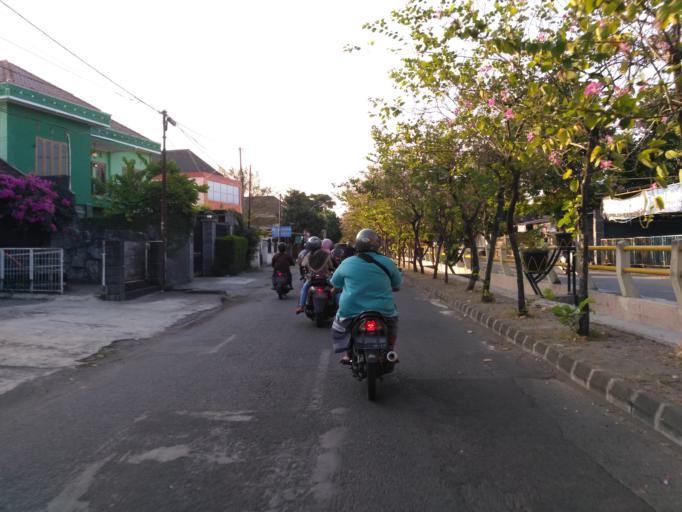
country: ID
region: Daerah Istimewa Yogyakarta
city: Yogyakarta
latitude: -7.8073
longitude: 110.3817
